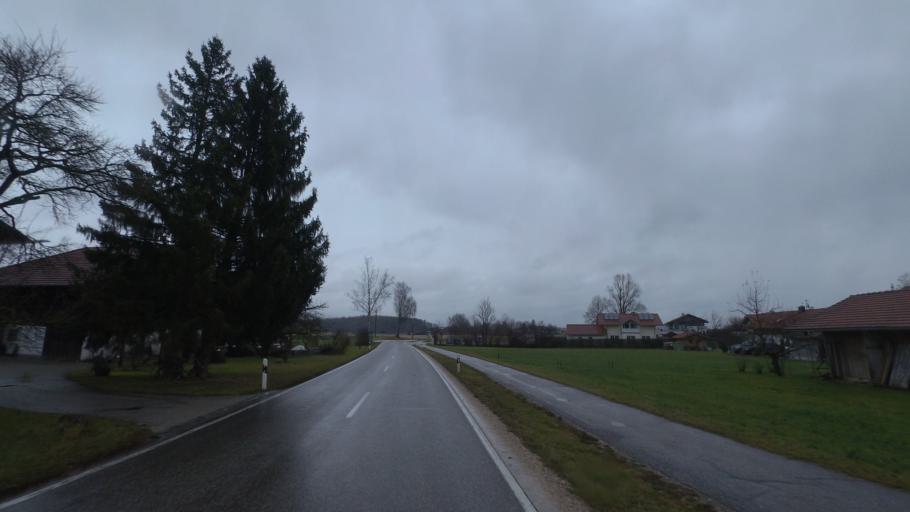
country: DE
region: Bavaria
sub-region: Upper Bavaria
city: Petting
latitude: 47.9417
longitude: 12.8035
